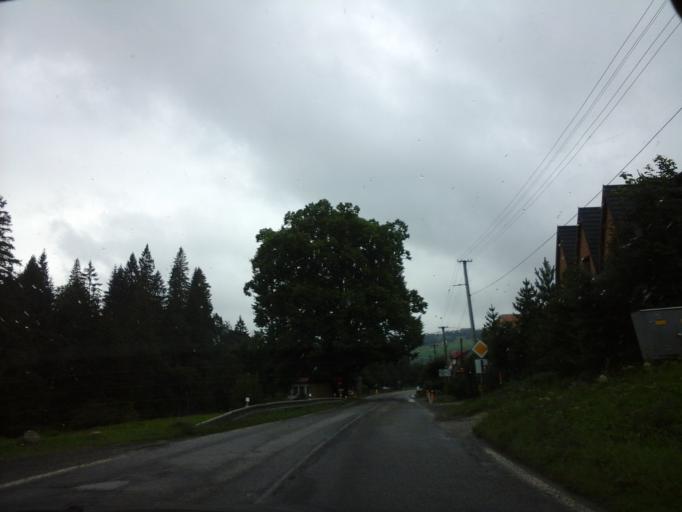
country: SK
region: Presovsky
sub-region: Okres Poprad
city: Zdiar
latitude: 49.2668
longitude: 20.2859
